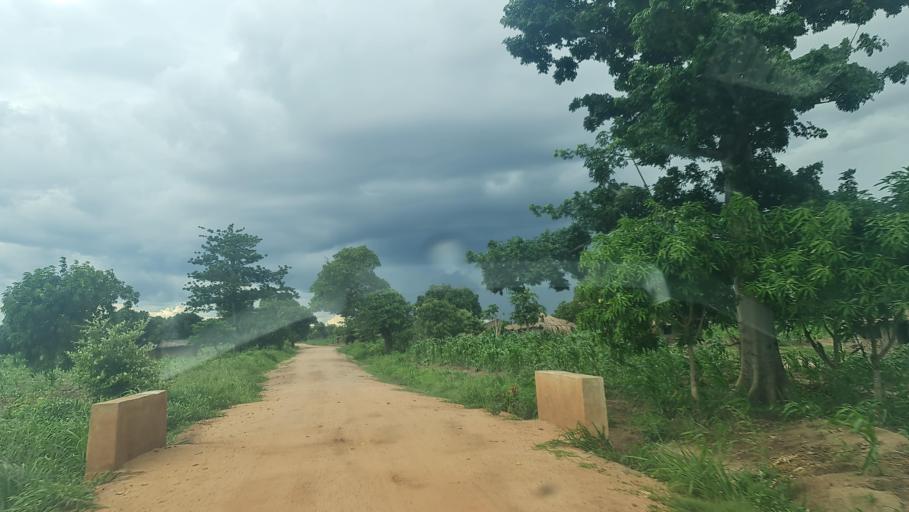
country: MW
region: Southern Region
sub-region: Nsanje District
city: Nsanje
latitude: -17.3775
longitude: 35.5842
